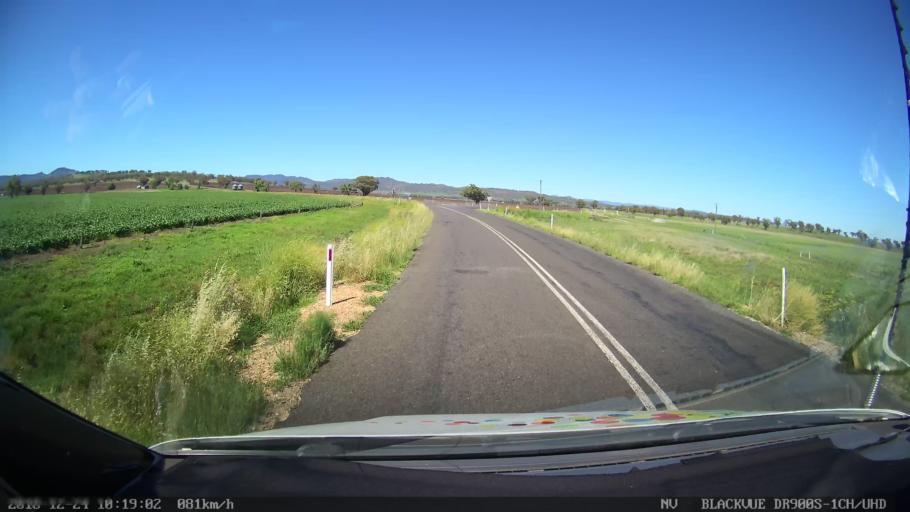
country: AU
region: New South Wales
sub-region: Liverpool Plains
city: Quirindi
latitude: -31.7263
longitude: 150.5677
